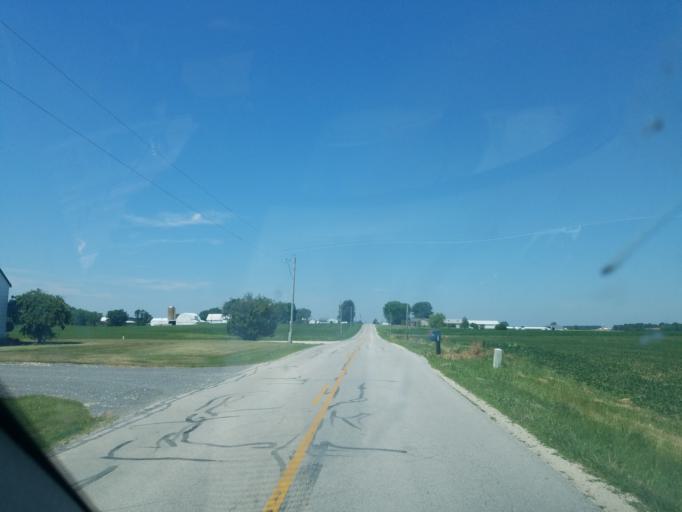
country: US
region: Ohio
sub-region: Mercer County
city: Saint Henry
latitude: 40.4506
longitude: -84.6965
